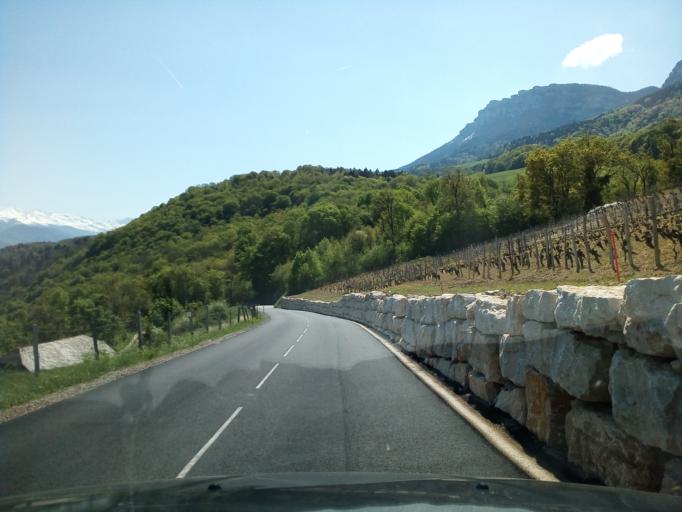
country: FR
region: Rhone-Alpes
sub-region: Departement de l'Isere
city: Chapareillan
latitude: 45.4773
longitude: 5.9759
